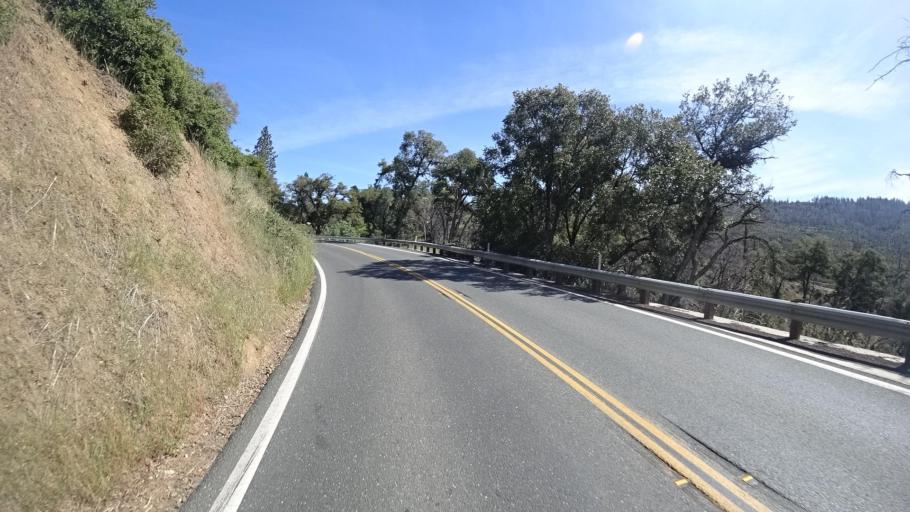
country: US
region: California
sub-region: Lake County
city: Cobb
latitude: 38.8090
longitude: -122.7094
